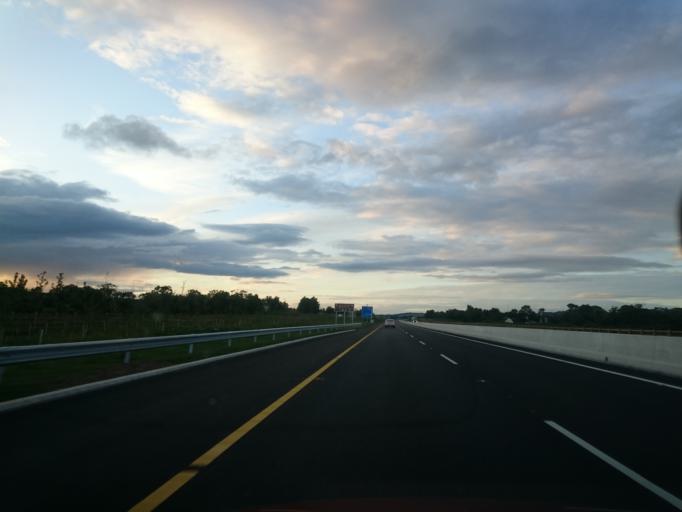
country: IE
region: Leinster
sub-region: Wicklow
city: Arklow
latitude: 52.8649
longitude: -6.1048
